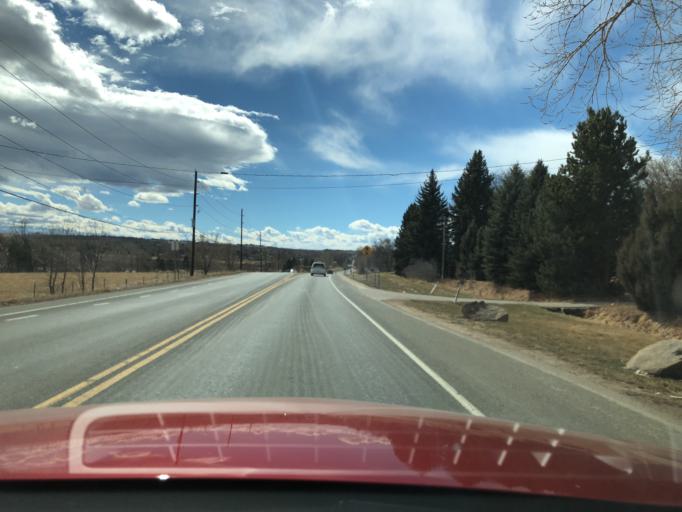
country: US
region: Colorado
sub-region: Boulder County
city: Gunbarrel
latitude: 40.0176
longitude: -105.1783
